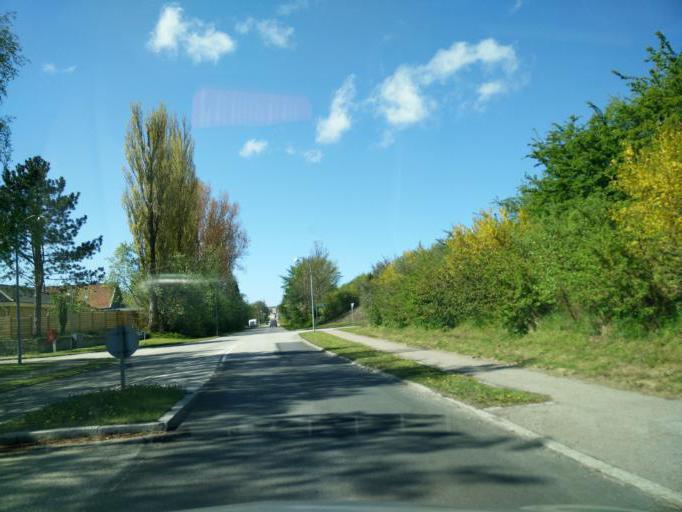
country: DK
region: Capital Region
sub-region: Gribskov Kommune
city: Helsinge
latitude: 56.0125
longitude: 12.2119
